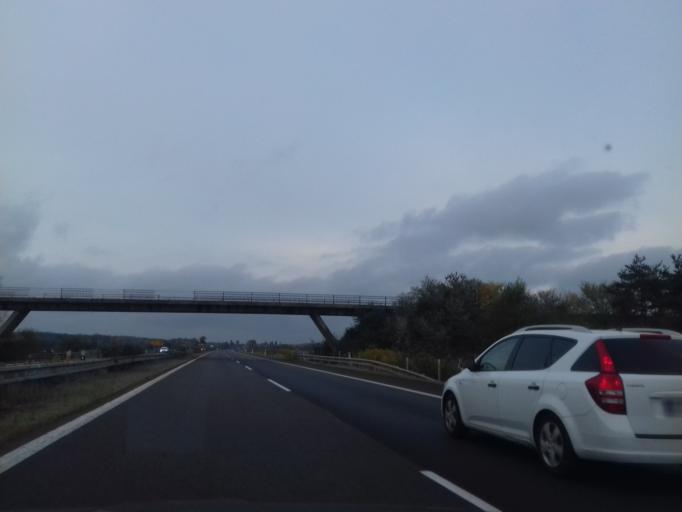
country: CZ
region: South Moravian
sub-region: Okres Breclav
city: Lanzhot
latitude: 48.6590
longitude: 16.9919
